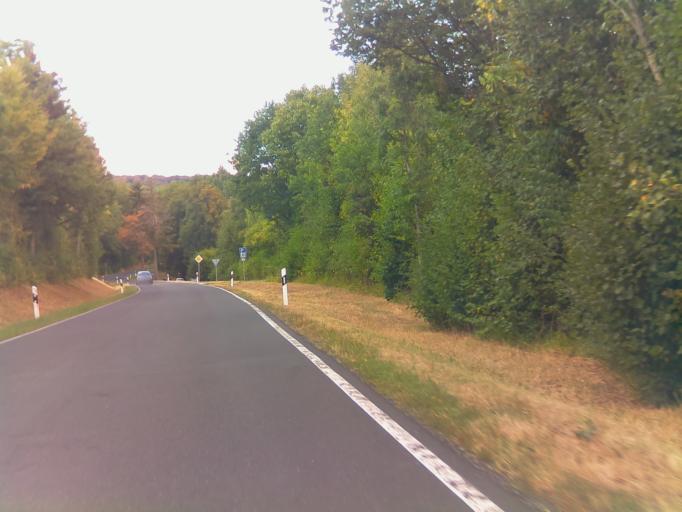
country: DE
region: Bavaria
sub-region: Regierungsbezirk Unterfranken
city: Oberelsbach
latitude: 50.4676
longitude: 10.0982
